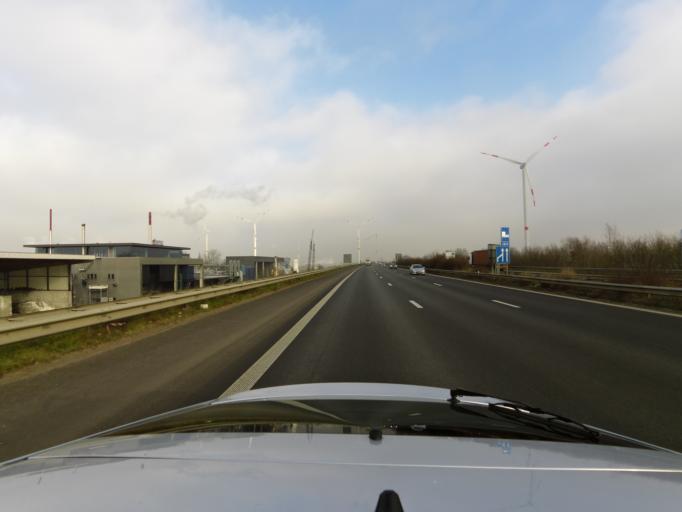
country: BE
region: Flanders
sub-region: Provincie West-Vlaanderen
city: Izegem
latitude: 50.9332
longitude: 3.1724
